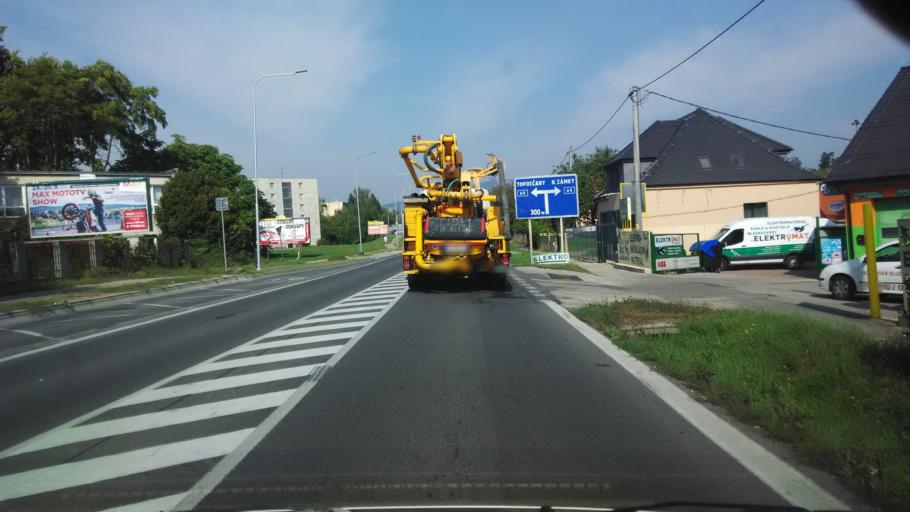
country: SK
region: Nitriansky
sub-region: Okres Nitra
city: Nitra
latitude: 48.2934
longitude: 18.0775
